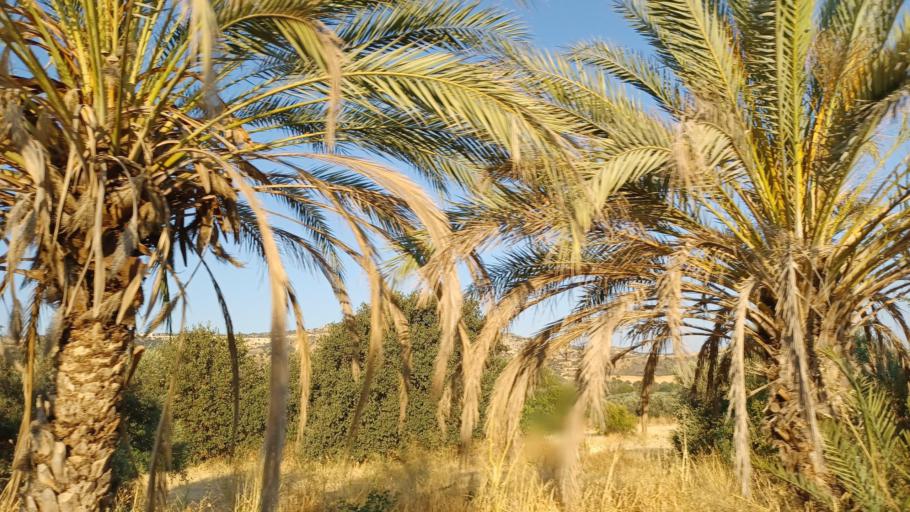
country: CY
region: Pafos
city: Polis
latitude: 35.0018
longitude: 32.4421
